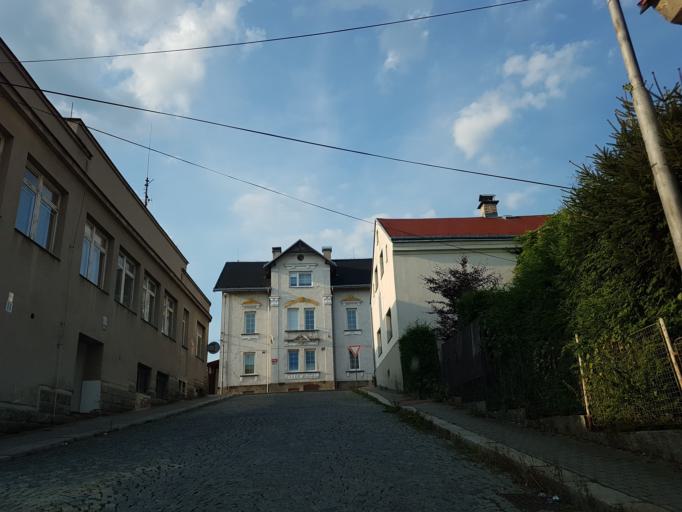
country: CZ
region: Liberecky
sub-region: Okres Jablonec nad Nisou
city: Jablonec nad Nisou
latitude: 50.7253
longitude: 15.1810
